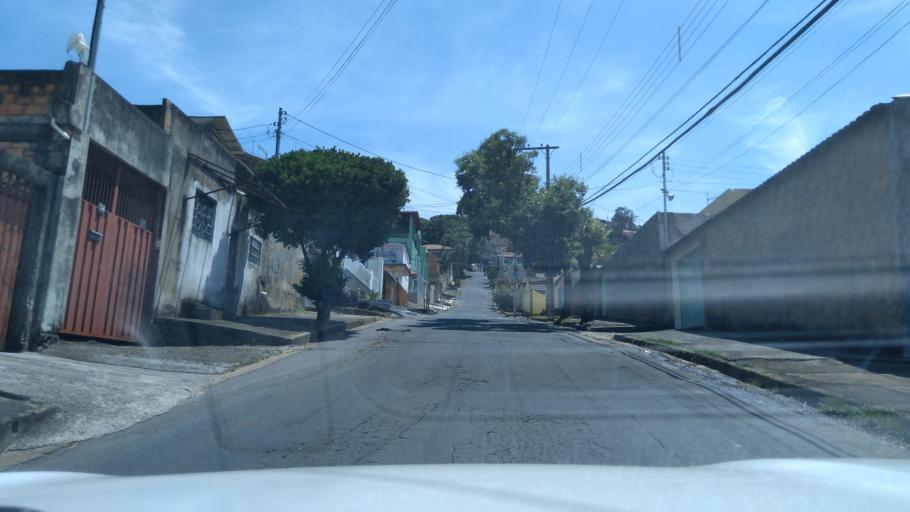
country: BR
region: Minas Gerais
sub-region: Contagem
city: Contagem
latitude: -19.9085
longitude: -44.0154
